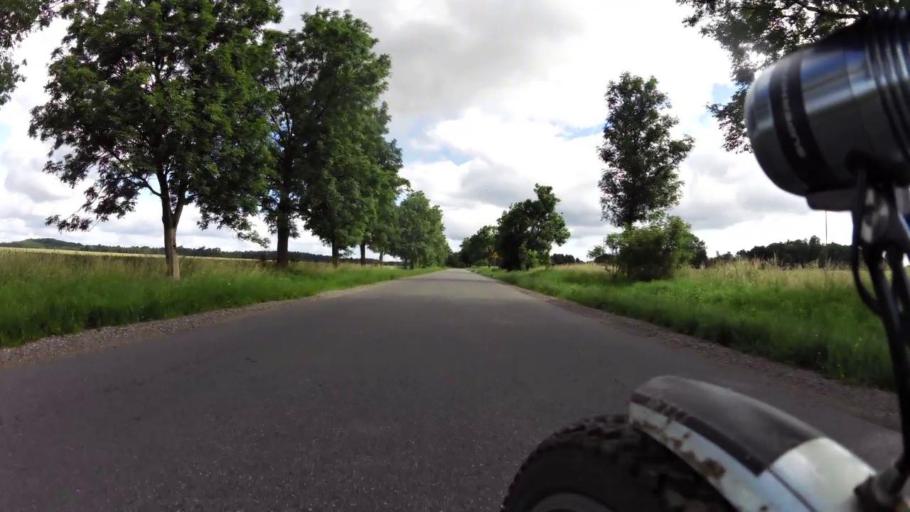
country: PL
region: West Pomeranian Voivodeship
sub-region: Powiat swidwinski
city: Rabino
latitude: 53.7926
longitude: 15.9052
